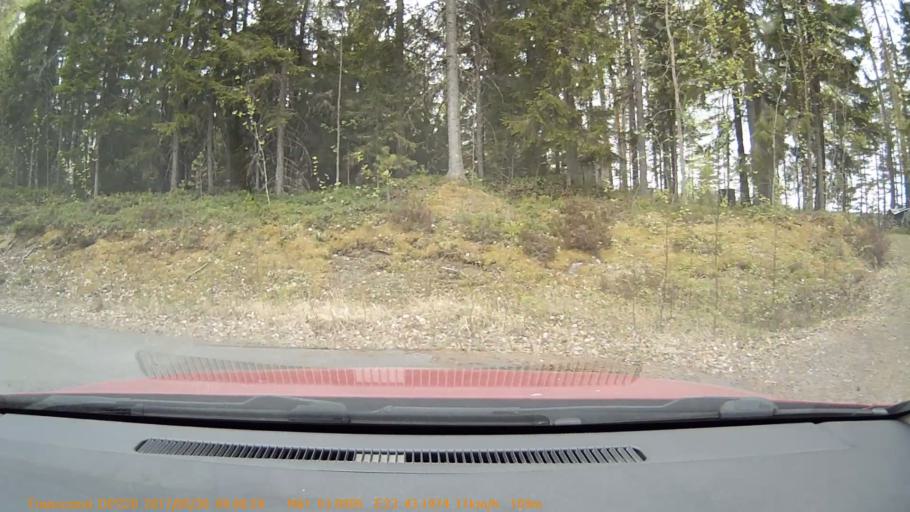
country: FI
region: Pirkanmaa
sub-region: Tampere
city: Kuru
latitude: 61.8849
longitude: 23.7200
